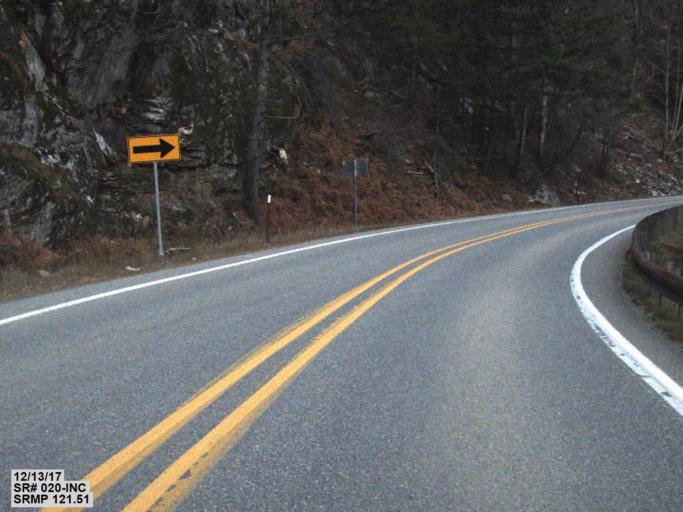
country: US
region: Washington
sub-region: Snohomish County
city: Darrington
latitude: 48.6846
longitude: -121.2419
